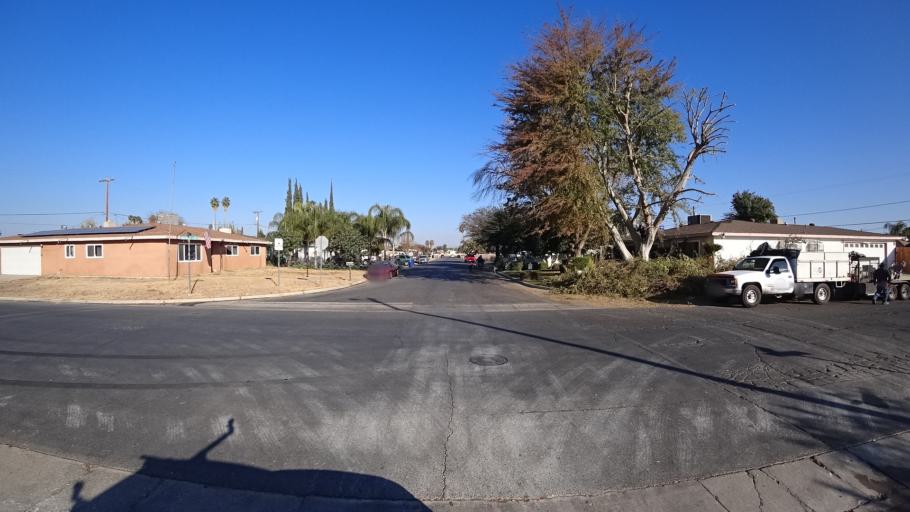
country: US
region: California
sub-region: Kern County
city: Greenfield
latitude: 35.3007
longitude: -119.0168
